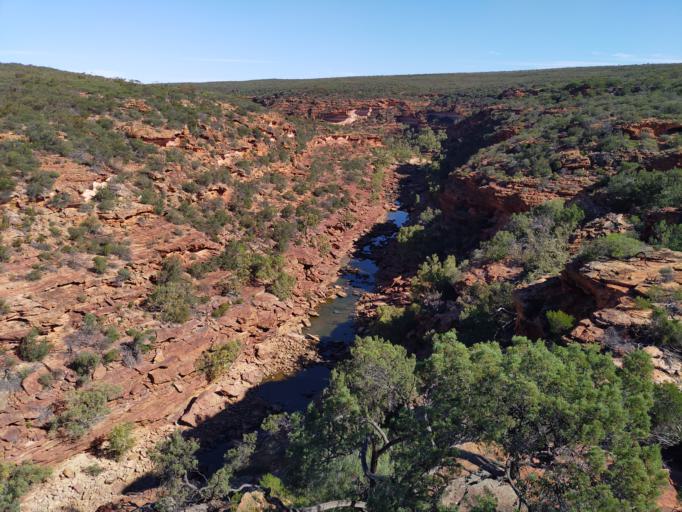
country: AU
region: Western Australia
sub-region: Northampton Shire
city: Kalbarri
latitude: -27.6537
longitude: 114.4566
